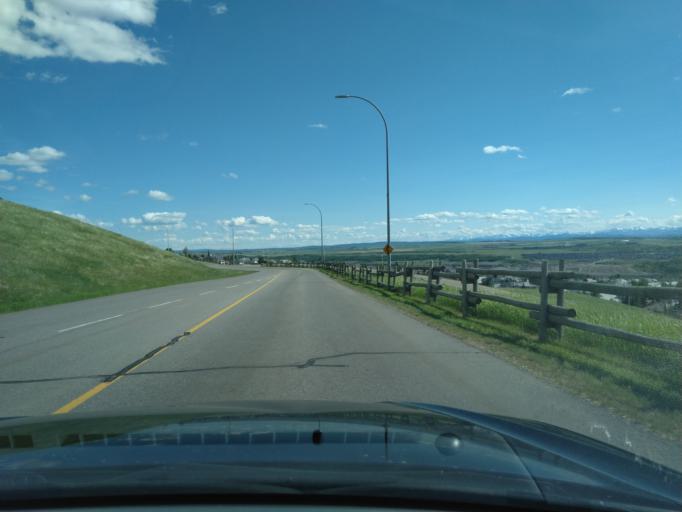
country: CA
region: Alberta
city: Cochrane
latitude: 51.1905
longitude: -114.4307
